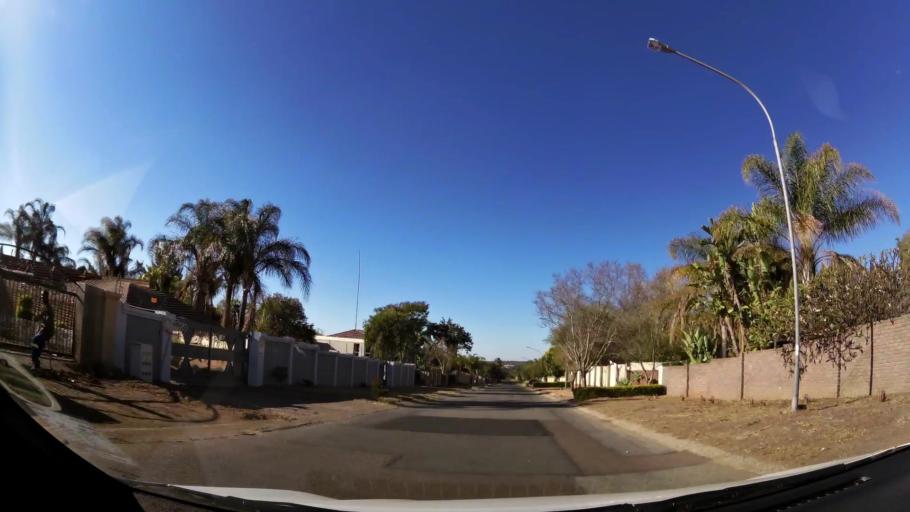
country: ZA
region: Limpopo
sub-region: Capricorn District Municipality
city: Polokwane
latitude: -23.8829
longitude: 29.4886
